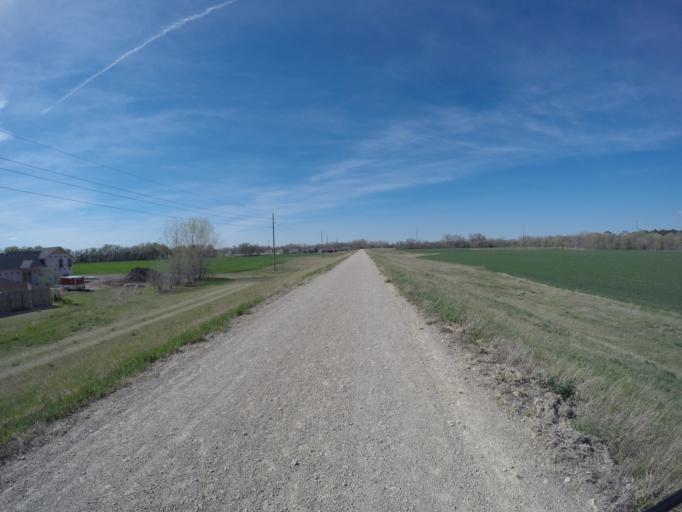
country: US
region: Kansas
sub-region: Saline County
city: Salina
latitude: 38.8027
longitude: -97.5822
